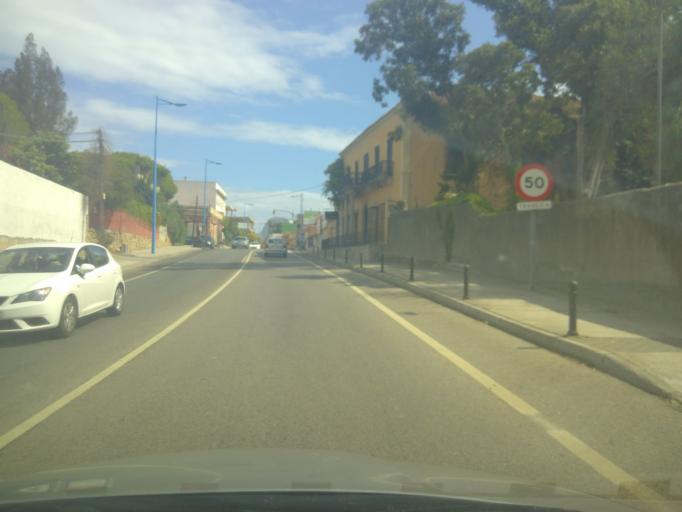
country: ES
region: Andalusia
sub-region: Provincia de Cadiz
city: San Roque
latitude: 36.1796
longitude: -5.3793
